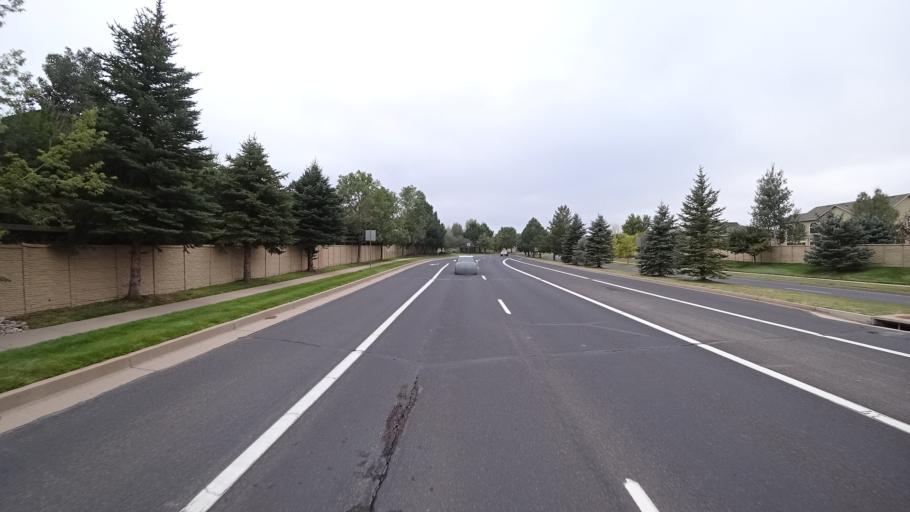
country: US
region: Colorado
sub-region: El Paso County
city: Cimarron Hills
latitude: 38.9176
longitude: -104.6921
